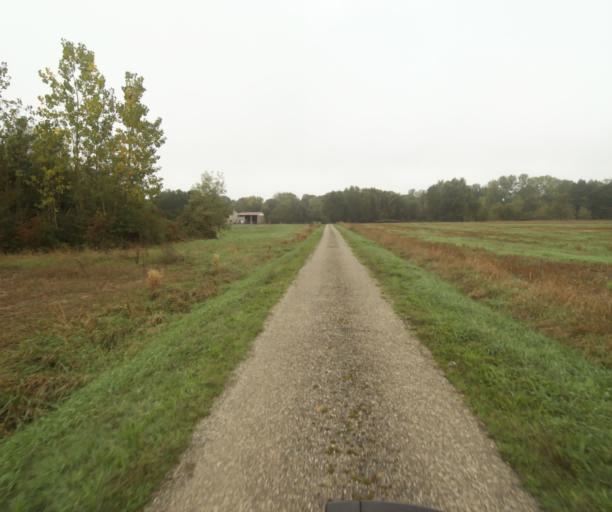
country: FR
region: Midi-Pyrenees
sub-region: Departement du Tarn-et-Garonne
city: Orgueil
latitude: 43.9088
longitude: 1.4180
